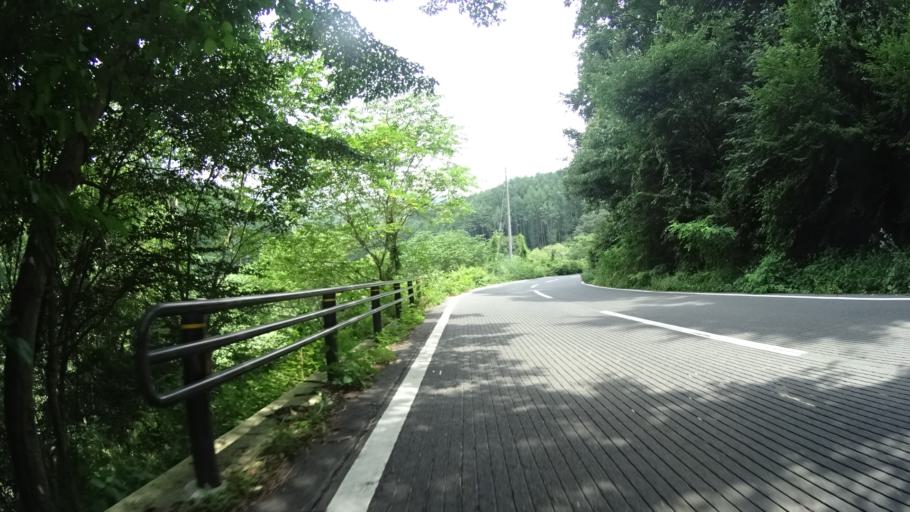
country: JP
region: Yamanashi
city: Nirasaki
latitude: 35.8827
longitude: 138.5215
